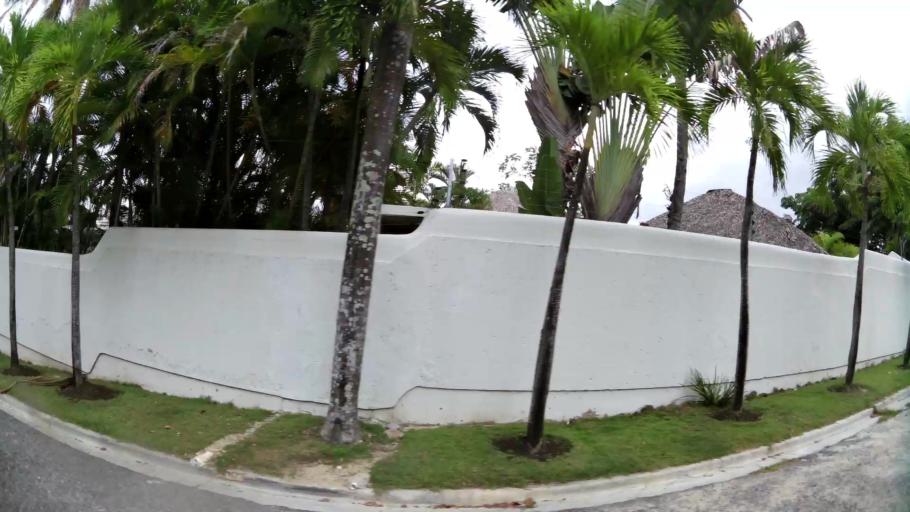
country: DO
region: Nacional
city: La Agustina
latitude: 18.5041
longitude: -69.9348
